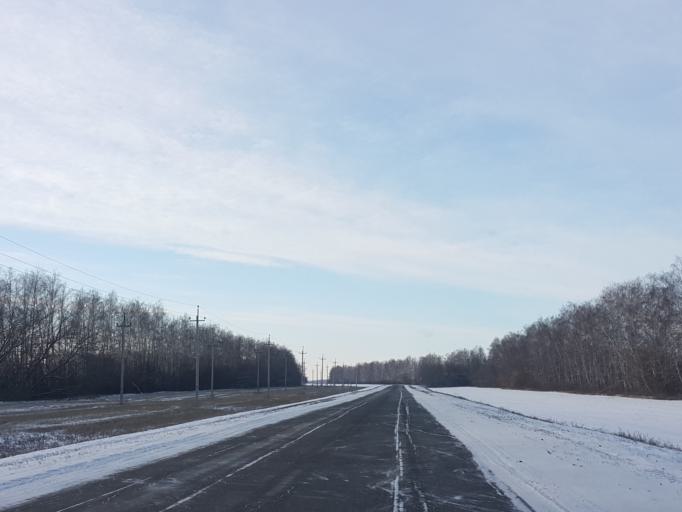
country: RU
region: Tambov
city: Znamenka
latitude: 52.4005
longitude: 41.3814
